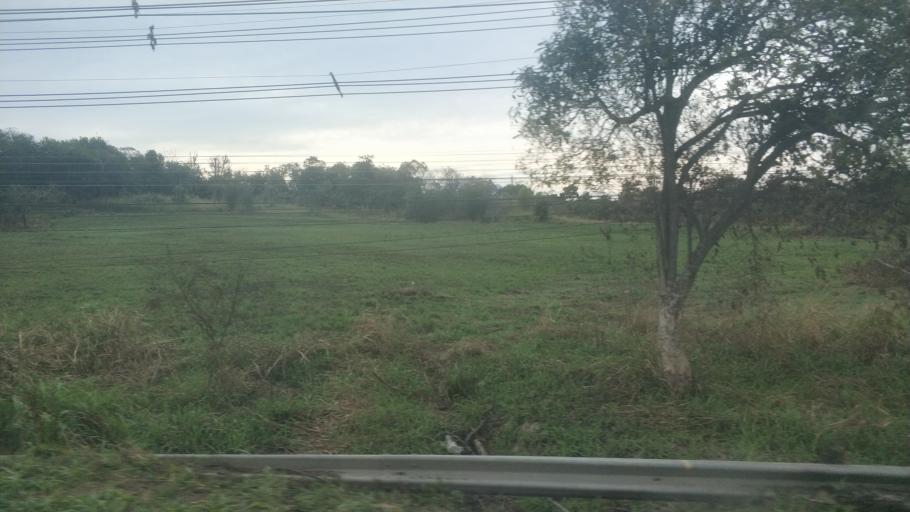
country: BR
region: Rio de Janeiro
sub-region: Seropedica
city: Seropedica
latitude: -22.7585
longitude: -43.6889
